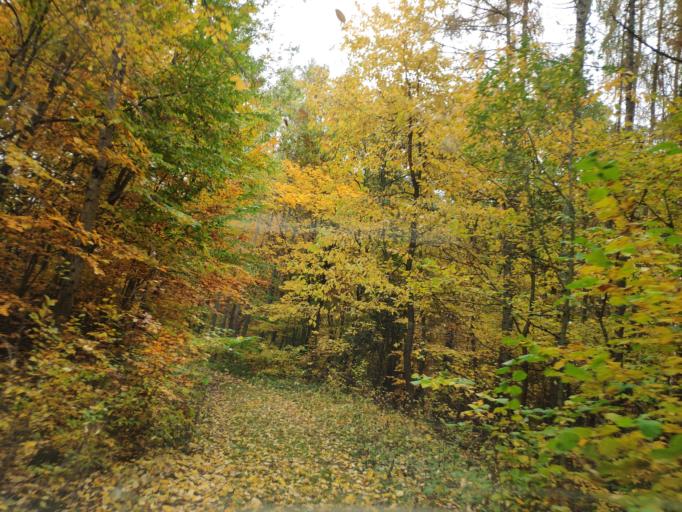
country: SK
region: Kosicky
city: Moldava nad Bodvou
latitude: 48.7236
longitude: 21.1001
